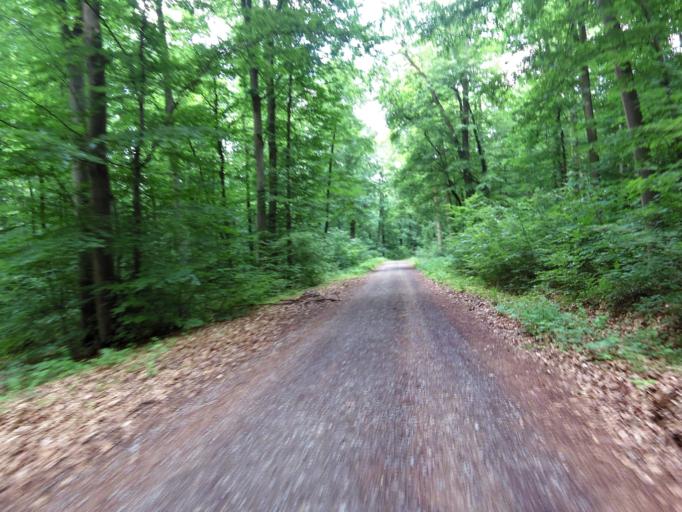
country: DE
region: Bavaria
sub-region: Regierungsbezirk Unterfranken
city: Wuerzburg
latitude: 49.7646
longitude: 9.8780
